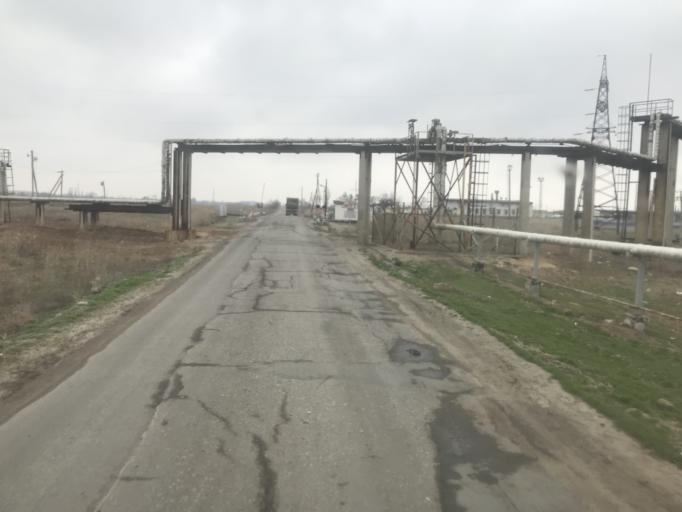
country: RU
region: Volgograd
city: Svetlyy Yar
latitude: 48.5135
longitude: 44.6343
